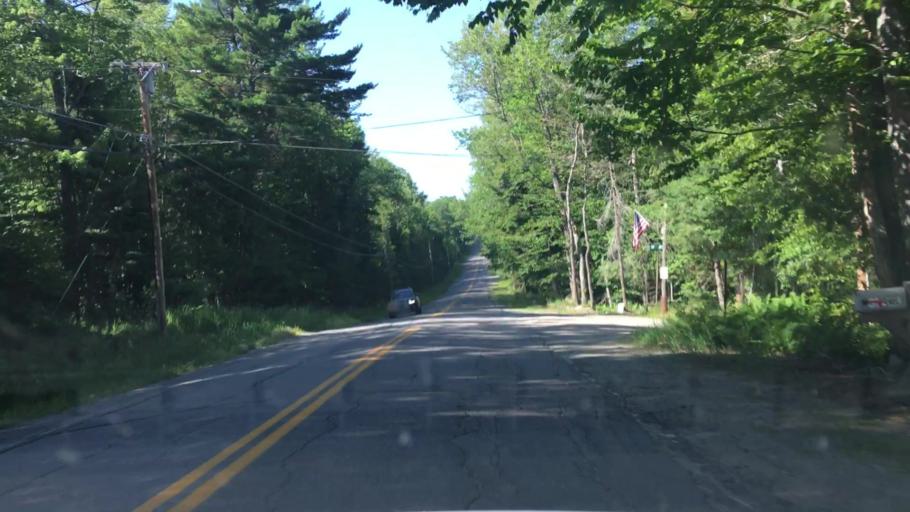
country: US
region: Maine
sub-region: Penobscot County
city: Enfield
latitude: 45.2700
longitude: -68.5614
